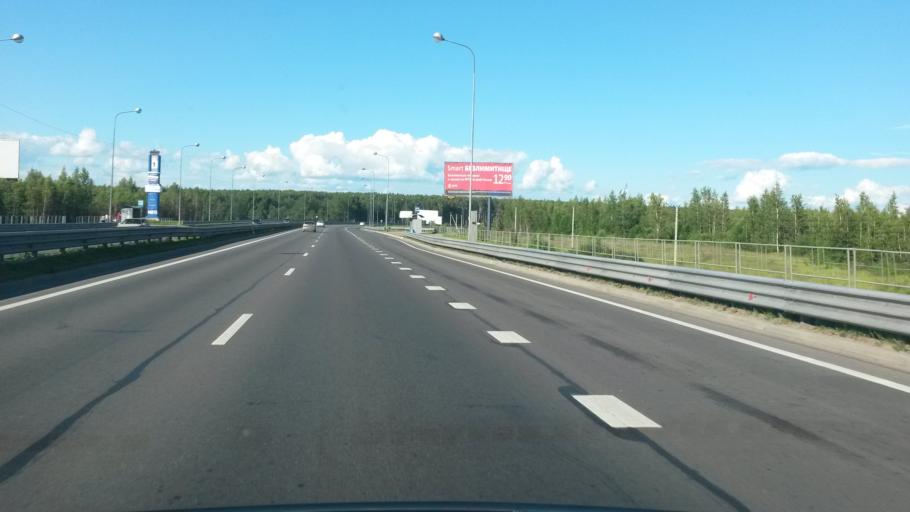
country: RU
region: Jaroslavl
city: Yaroslavl
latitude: 57.6802
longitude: 39.8709
